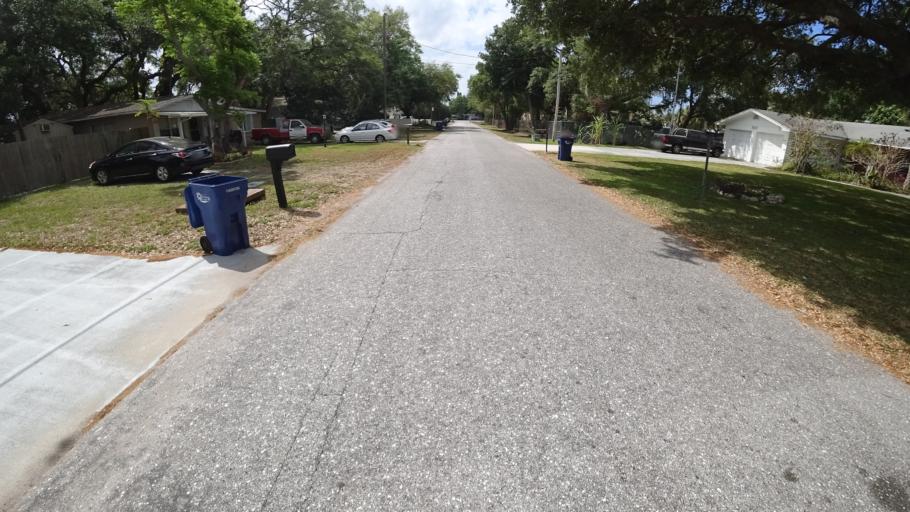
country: US
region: Florida
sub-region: Manatee County
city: Bayshore Gardens
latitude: 27.4418
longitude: -82.5865
